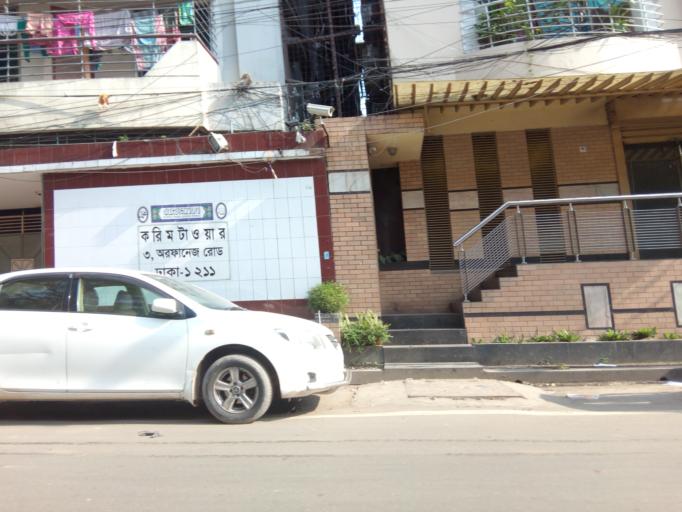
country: BD
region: Dhaka
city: Azimpur
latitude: 23.7223
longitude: 90.3914
